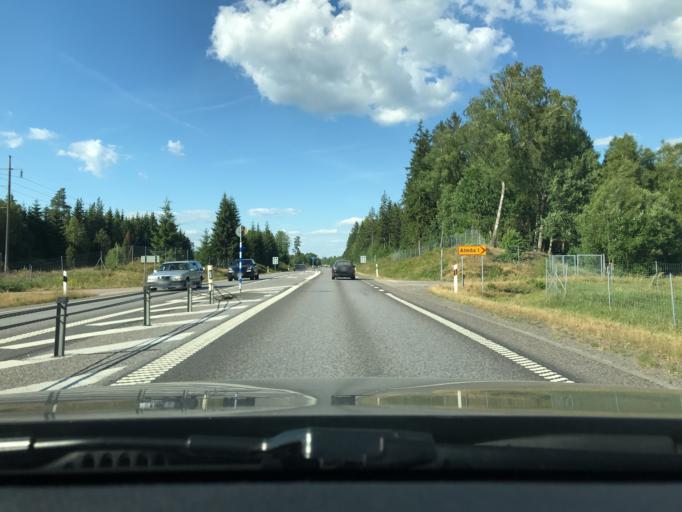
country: SE
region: Kronoberg
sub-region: Almhults Kommun
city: AElmhult
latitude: 56.5109
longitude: 14.1304
